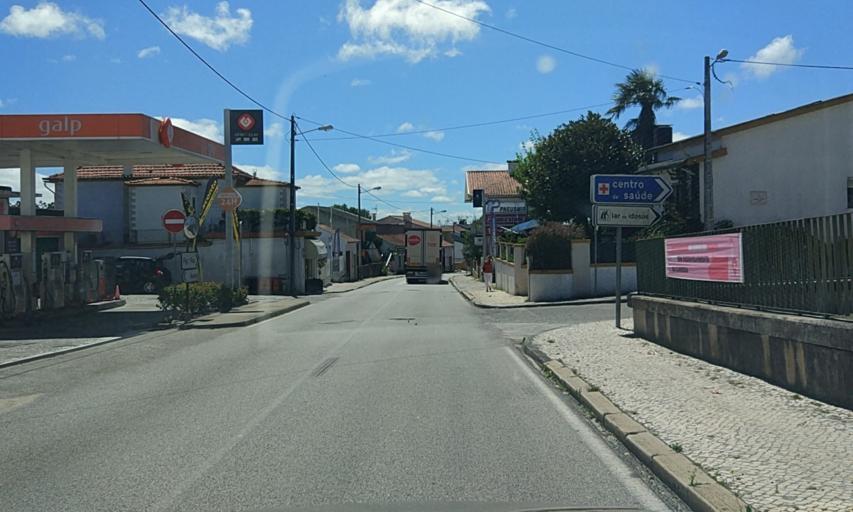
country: PT
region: Coimbra
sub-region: Mira
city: Mira
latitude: 40.4272
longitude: -8.7362
